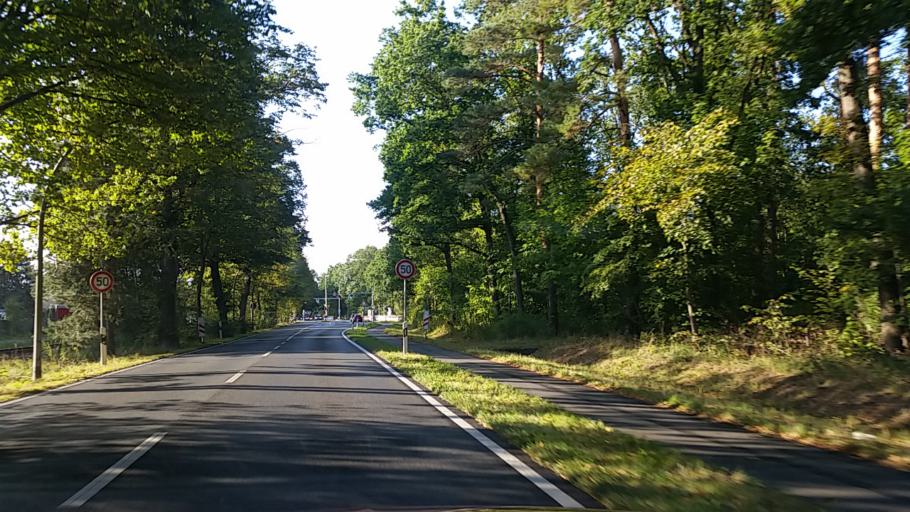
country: DE
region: Lower Saxony
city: Braunschweig
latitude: 52.3026
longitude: 10.5474
